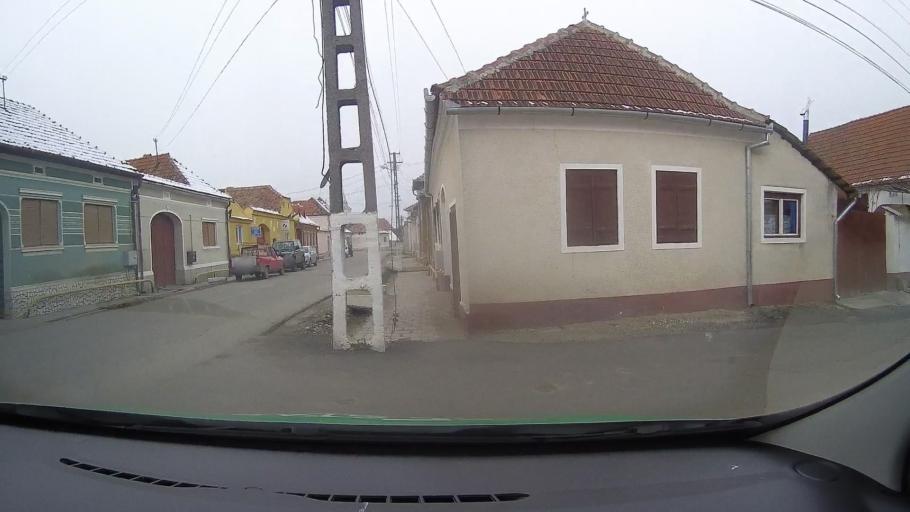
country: RO
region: Hunedoara
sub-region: Comuna Romos
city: Romos
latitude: 45.8423
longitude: 23.2747
